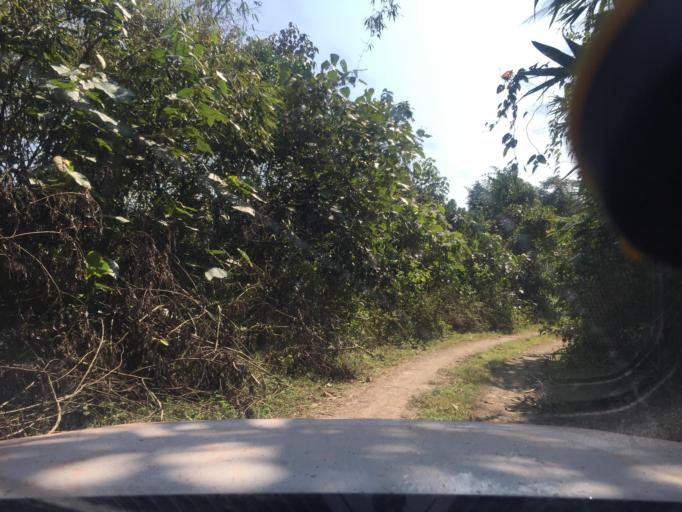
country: LA
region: Phongsali
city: Phongsali
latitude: 21.6890
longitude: 102.4091
